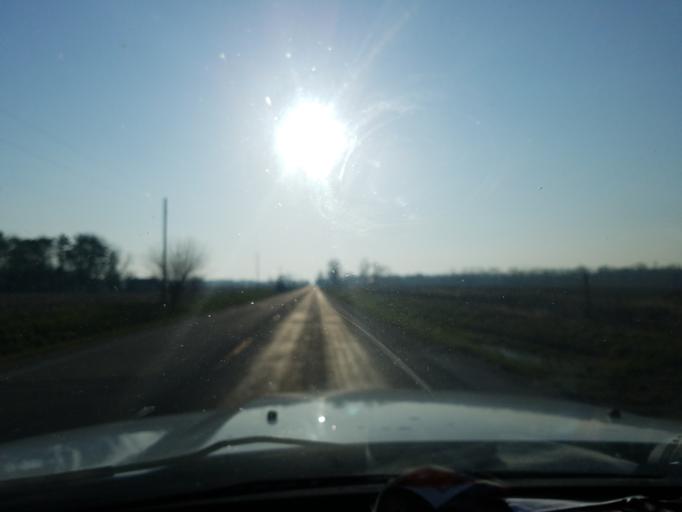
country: US
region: Indiana
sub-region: Vigo County
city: Seelyville
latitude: 39.3887
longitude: -87.1875
